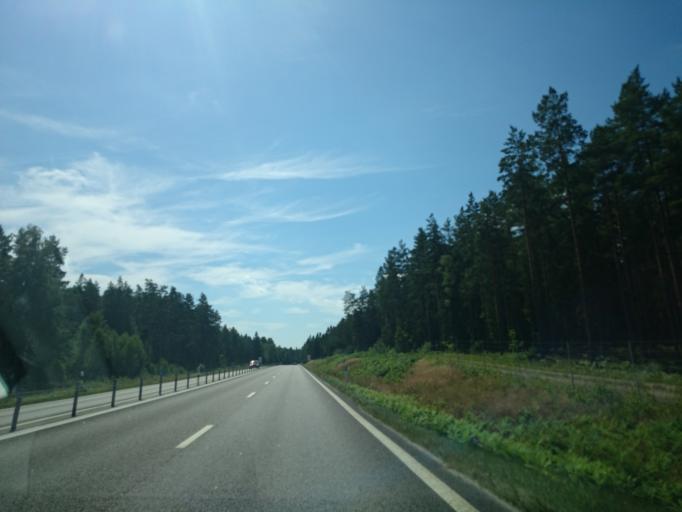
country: SE
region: Kalmar
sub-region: Monsteras Kommun
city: Timmernabben
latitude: 56.8759
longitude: 16.3825
